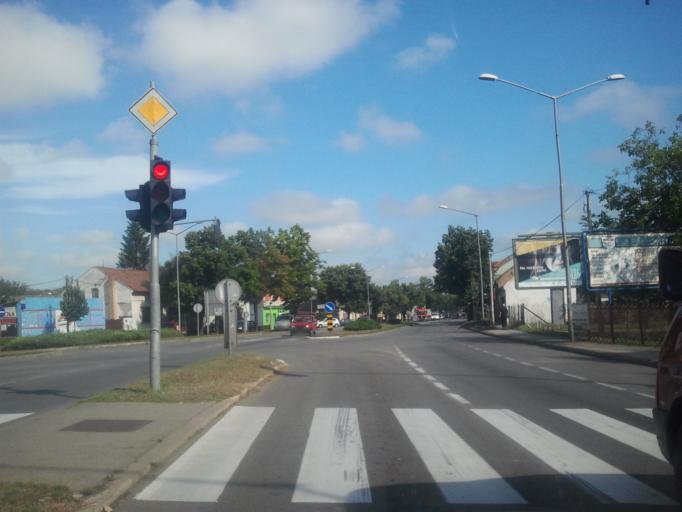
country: RS
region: Autonomna Pokrajina Vojvodina
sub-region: Juznobacki Okrug
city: Petrovaradin
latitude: 45.2424
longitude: 19.8824
